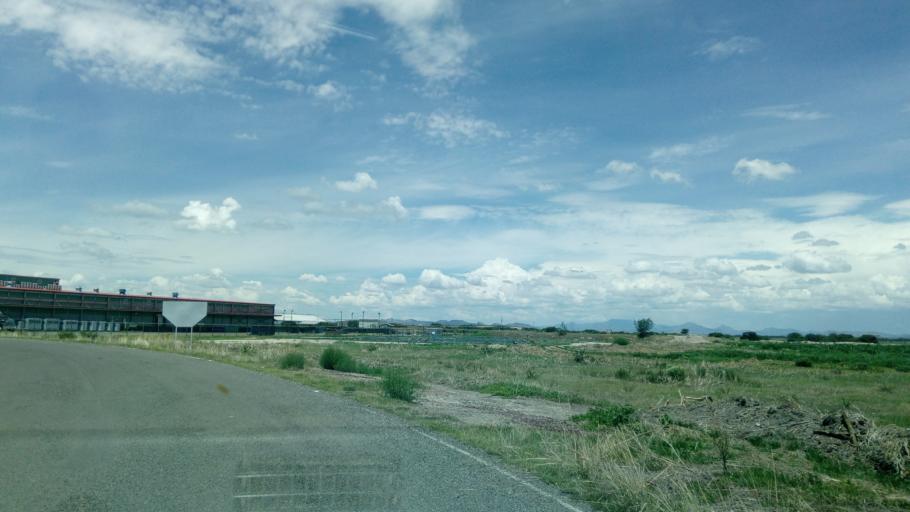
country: MX
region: Durango
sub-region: Durango
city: Jose Refugio Salcido
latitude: 24.1694
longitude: -104.4980
